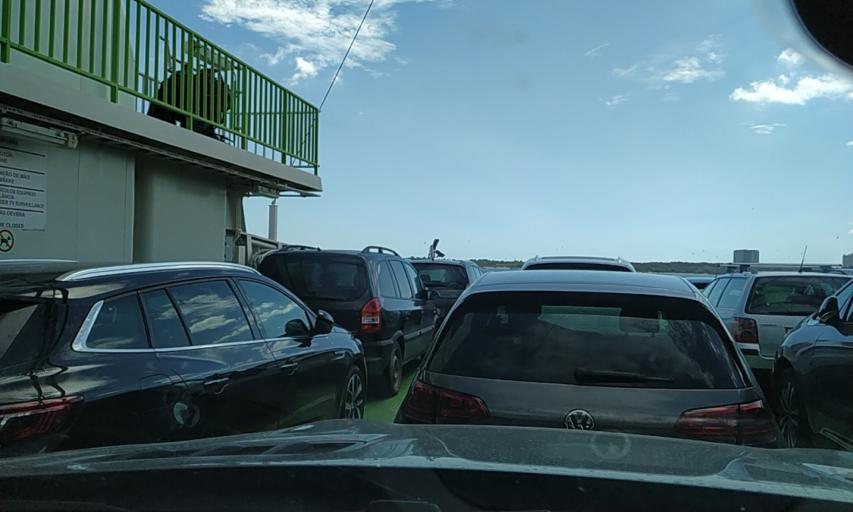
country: PT
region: Setubal
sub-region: Setubal
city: Setubal
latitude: 38.5009
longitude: -8.8870
